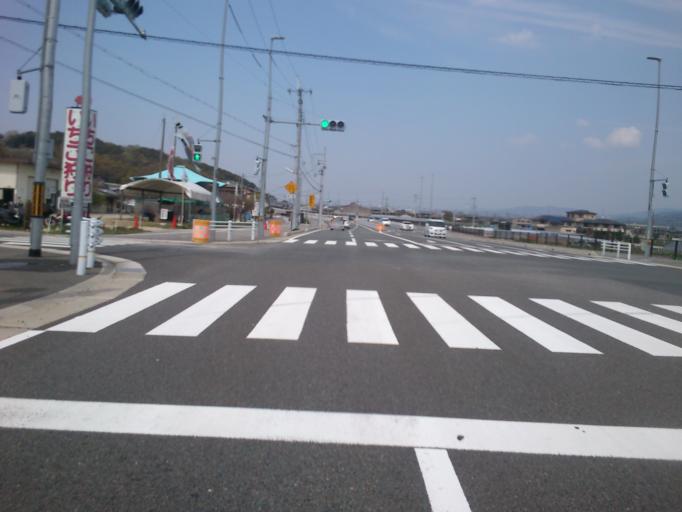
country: JP
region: Kyoto
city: Tanabe
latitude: 34.7696
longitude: 135.7879
